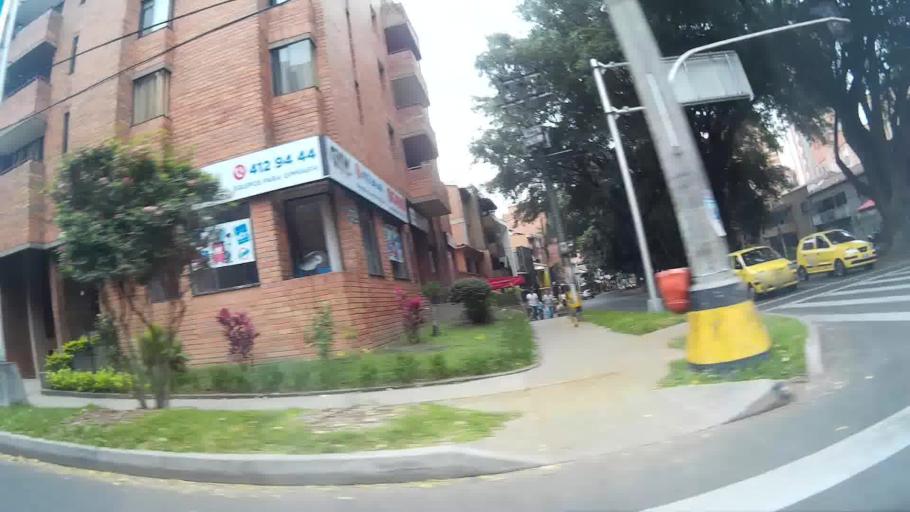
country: CO
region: Antioquia
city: Medellin
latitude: 6.2459
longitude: -75.5959
